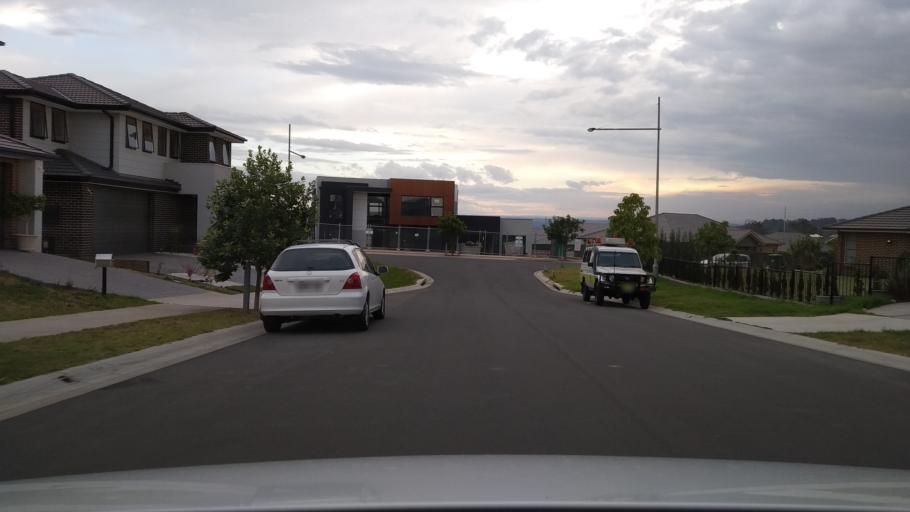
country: AU
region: New South Wales
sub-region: Camden
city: Narellan
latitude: -34.0032
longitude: 150.7282
